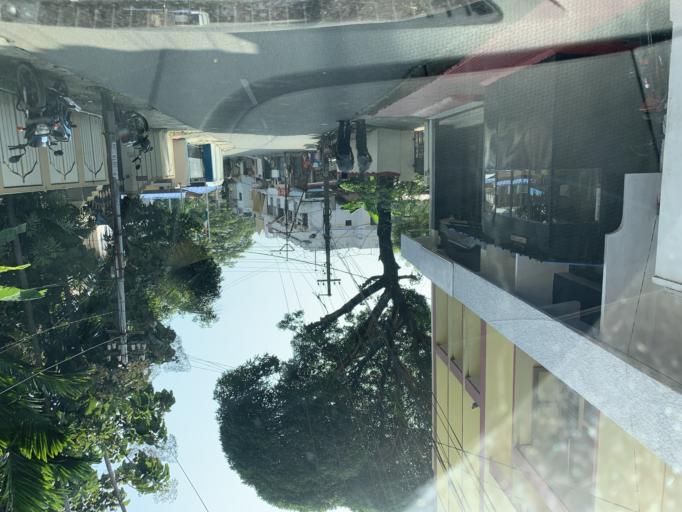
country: IN
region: Kerala
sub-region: Ernakulam
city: Cochin
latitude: 9.9600
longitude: 76.2574
